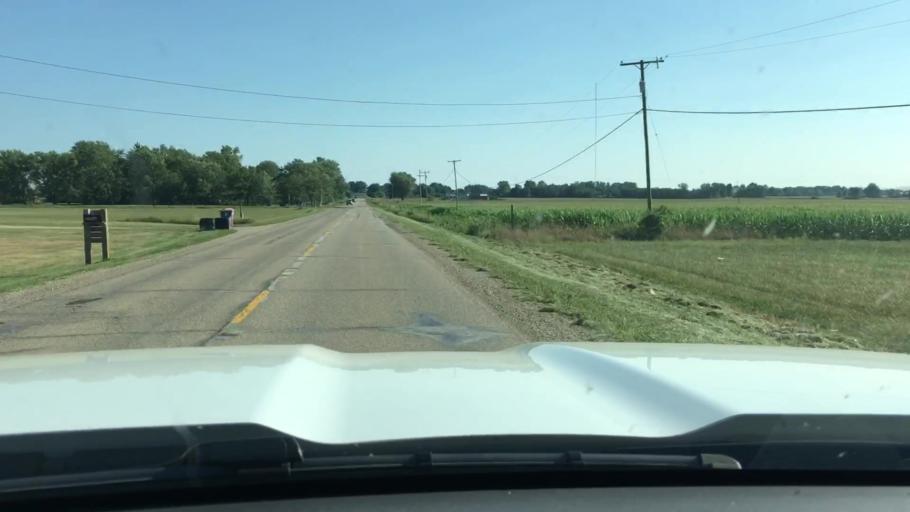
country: US
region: Michigan
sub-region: Ottawa County
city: Zeeland
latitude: 42.8659
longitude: -85.9602
